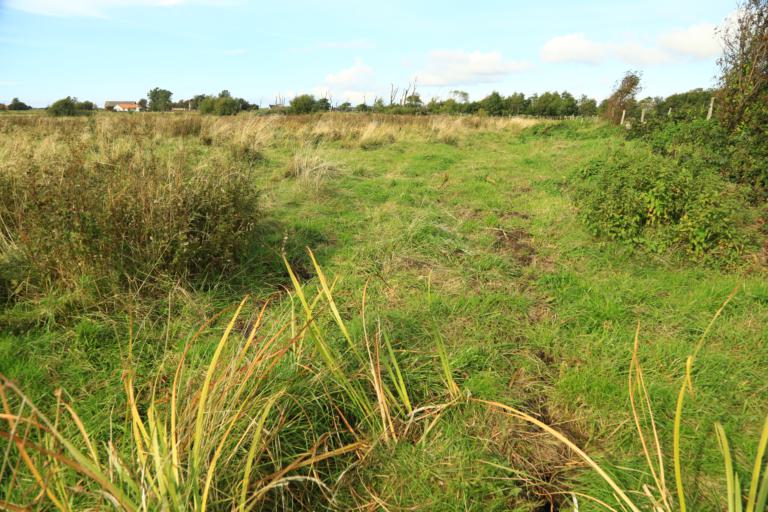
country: SE
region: Halland
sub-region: Varbergs Kommun
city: Traslovslage
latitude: 57.0247
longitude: 12.3331
